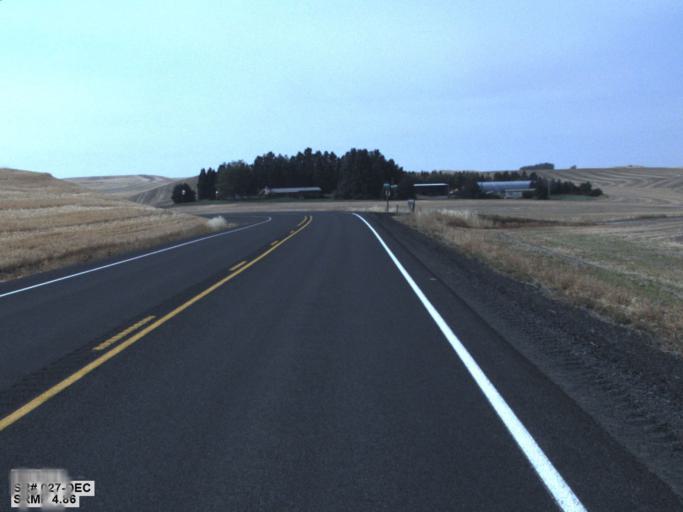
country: US
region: Washington
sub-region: Whitman County
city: Pullman
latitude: 46.7935
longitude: -117.1446
